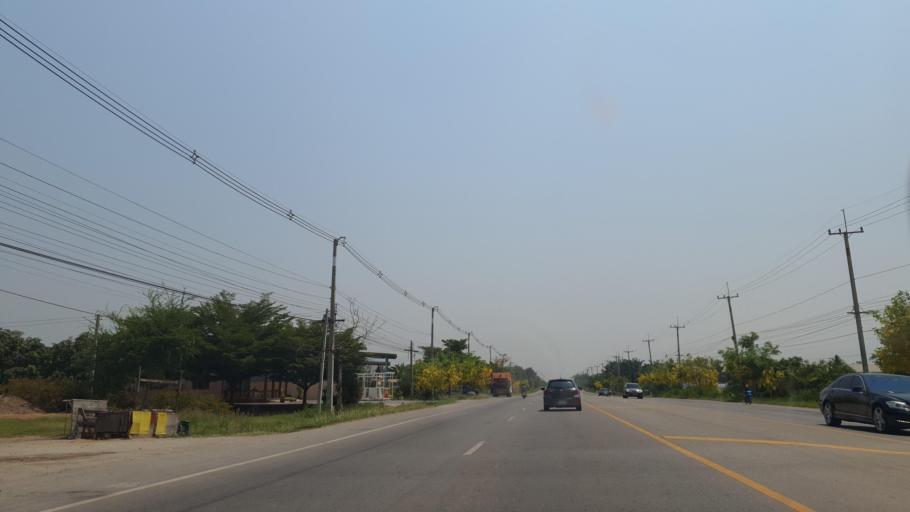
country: TH
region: Suphan Buri
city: U Thong
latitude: 14.2640
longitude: 99.8312
